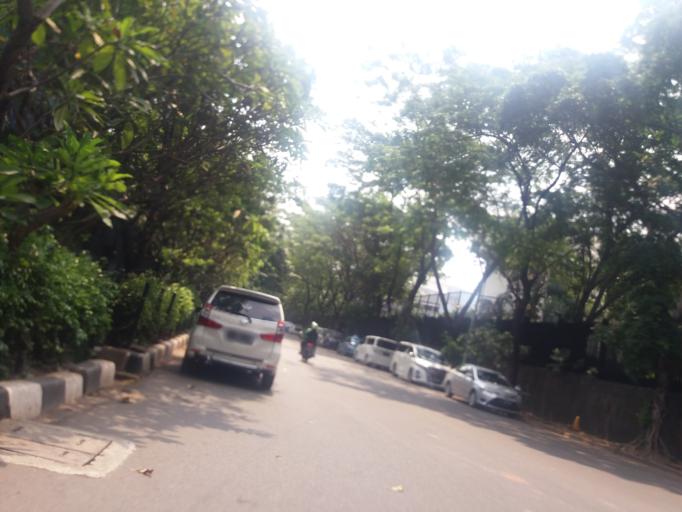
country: ID
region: Jakarta Raya
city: Jakarta
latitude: -6.2256
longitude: 106.8316
